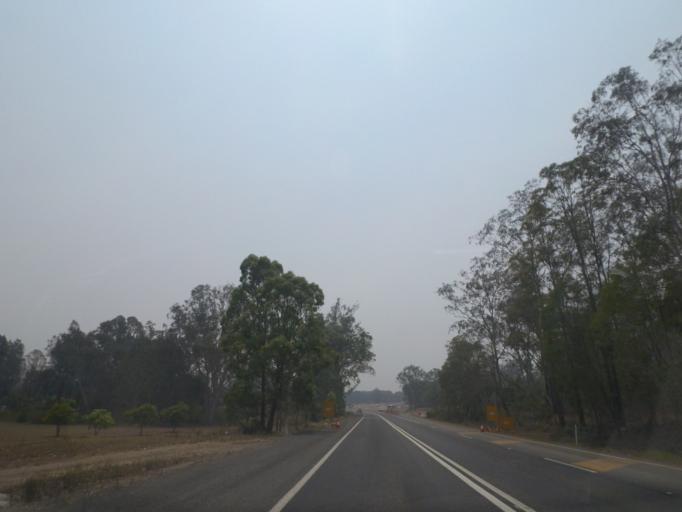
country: AU
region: New South Wales
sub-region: Clarence Valley
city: Maclean
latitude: -29.5527
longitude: 153.1537
